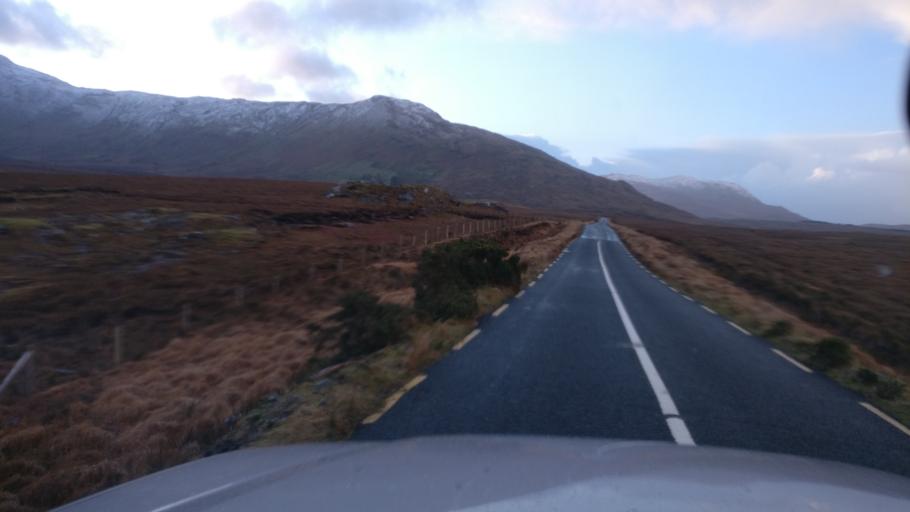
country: IE
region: Connaught
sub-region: County Galway
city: Clifden
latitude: 53.5303
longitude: -9.7606
